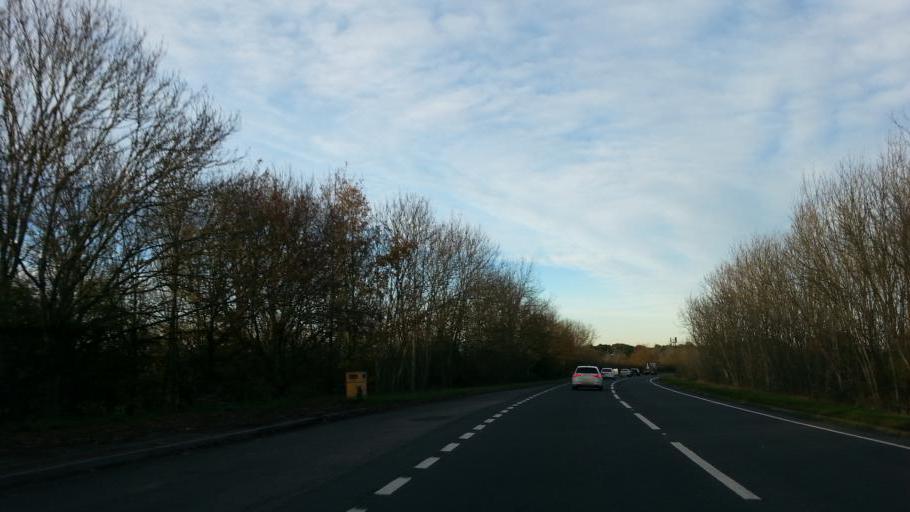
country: GB
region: England
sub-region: Northamptonshire
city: Broughton
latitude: 52.3716
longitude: -0.7843
